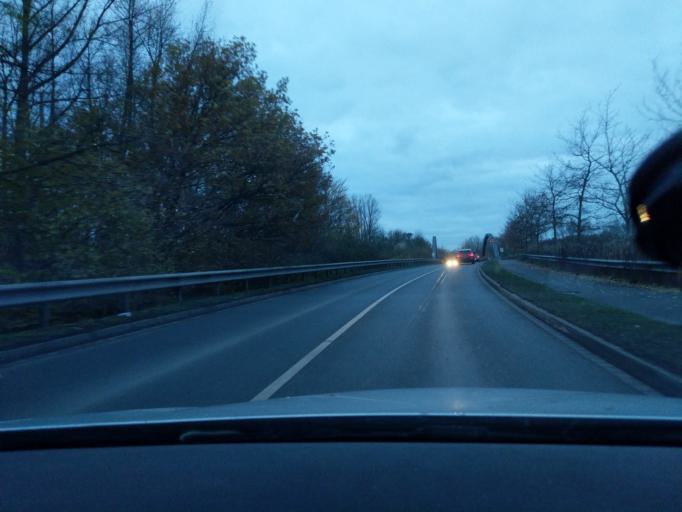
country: DE
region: North Rhine-Westphalia
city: Lunen
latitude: 51.6066
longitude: 7.4799
